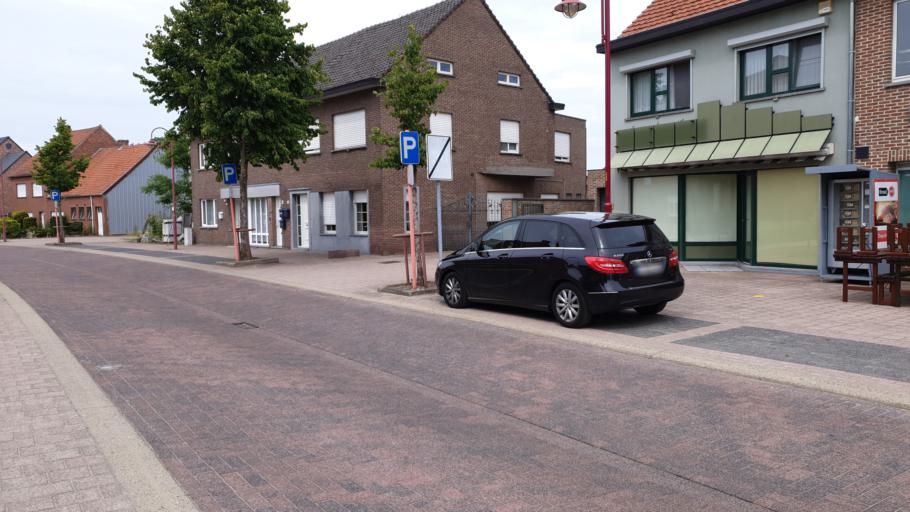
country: BE
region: Flanders
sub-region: Provincie Antwerpen
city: Meerhout
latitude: 51.1631
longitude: 5.0628
